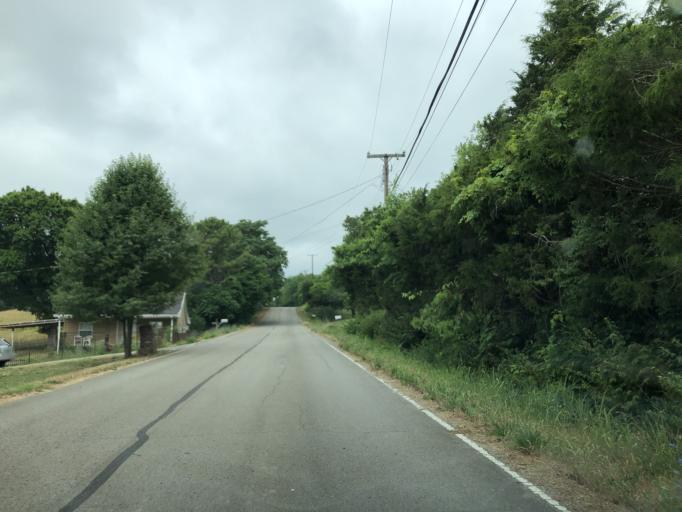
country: US
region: Tennessee
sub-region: Davidson County
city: Goodlettsville
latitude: 36.2899
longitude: -86.7498
